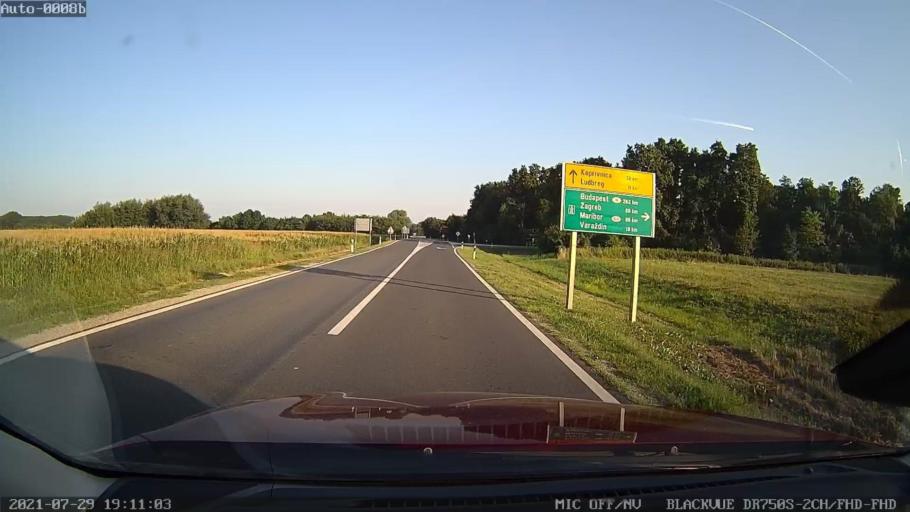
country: HR
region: Varazdinska
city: Jalzabet
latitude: 46.2827
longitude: 16.5063
